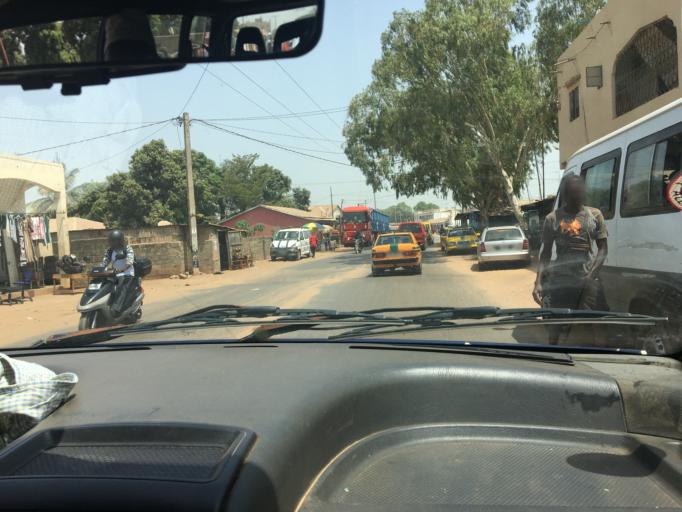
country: GM
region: Western
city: Abuko
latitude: 13.3963
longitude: -16.6735
